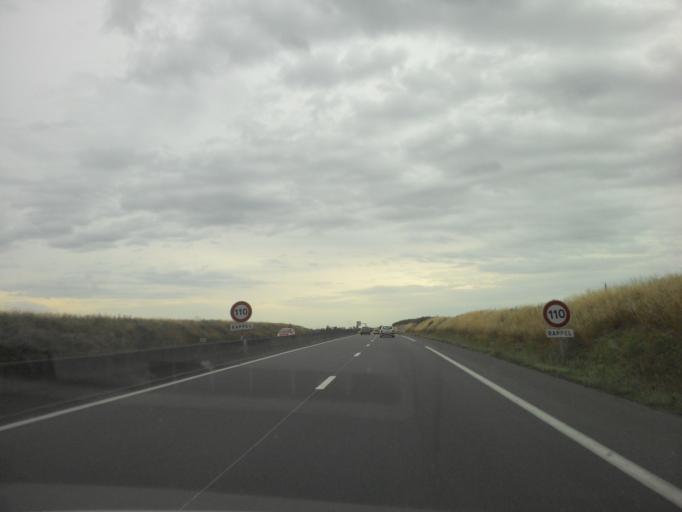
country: FR
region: Auvergne
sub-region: Departement du Puy-de-Dome
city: Menetrol
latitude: 45.8839
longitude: 3.1341
